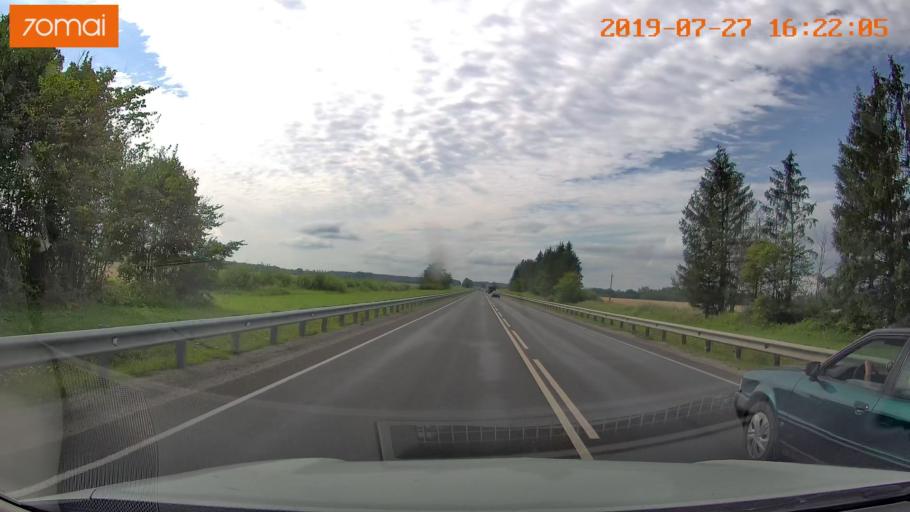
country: RU
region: Kaliningrad
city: Chernyakhovsk
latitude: 54.6266
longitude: 21.5032
